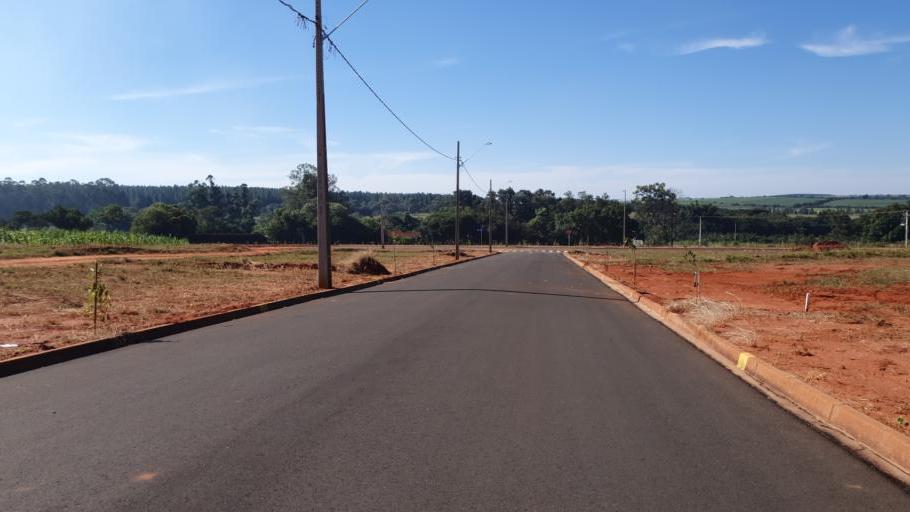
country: BR
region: Sao Paulo
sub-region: Paraguacu Paulista
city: Paraguacu Paulista
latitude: -22.3981
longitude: -50.5759
